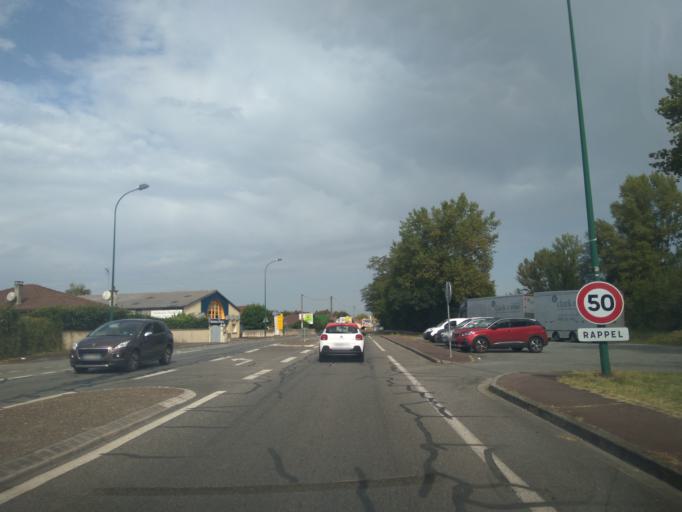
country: FR
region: Aquitaine
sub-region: Departement des Pyrenees-Atlantiques
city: Artiguelouve
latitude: 43.3090
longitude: -0.4480
